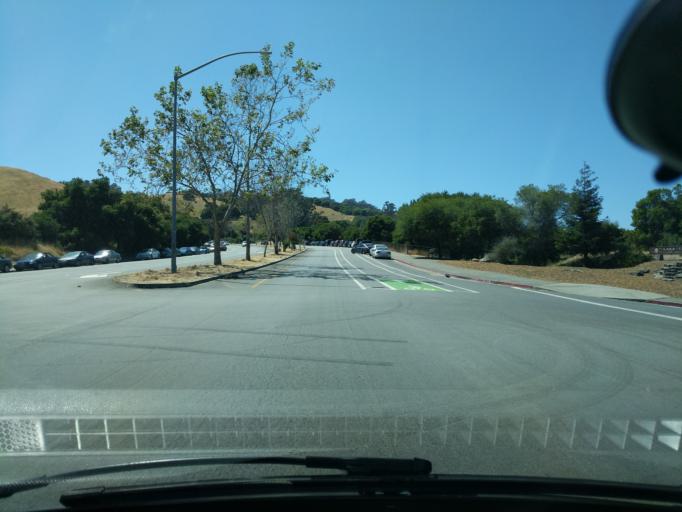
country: US
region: California
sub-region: Alameda County
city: Ashland
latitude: 37.7145
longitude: -122.1020
